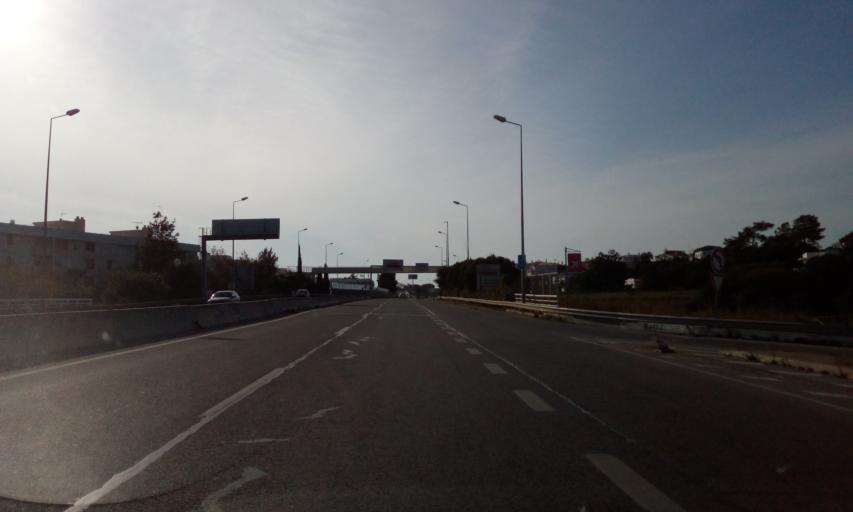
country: PT
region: Faro
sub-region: Faro
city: Faro
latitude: 37.0380
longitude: -7.9537
